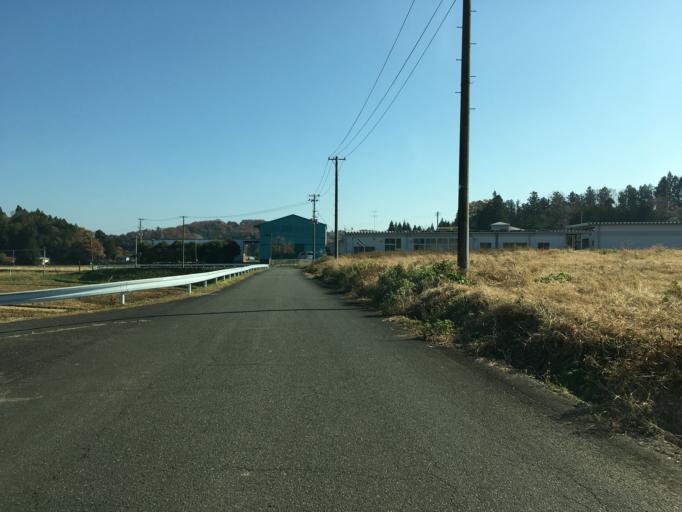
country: JP
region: Fukushima
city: Nihommatsu
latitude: 37.5727
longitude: 140.3870
